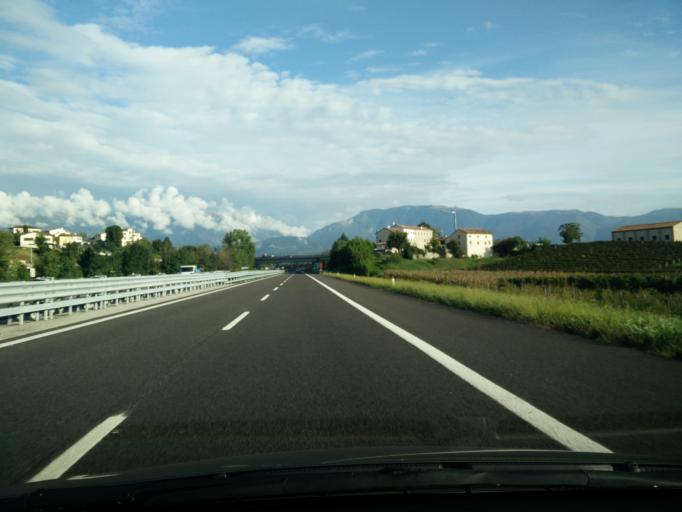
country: IT
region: Veneto
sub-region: Provincia di Treviso
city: Scomigo
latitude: 45.9304
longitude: 12.3131
